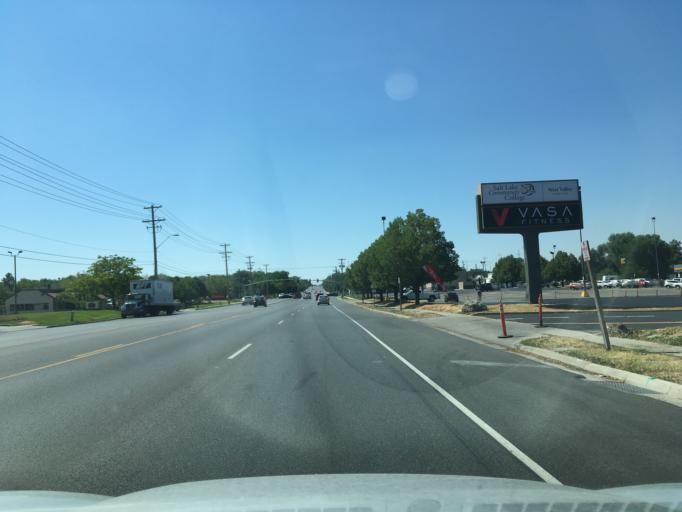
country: US
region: Utah
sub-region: Salt Lake County
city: West Valley City
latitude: 40.6985
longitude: -112.0250
